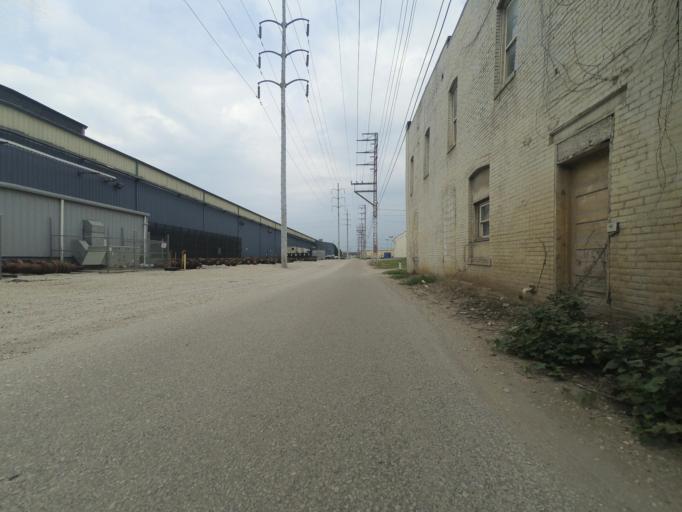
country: US
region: West Virginia
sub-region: Cabell County
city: Huntington
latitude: 38.4264
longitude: -82.4256
